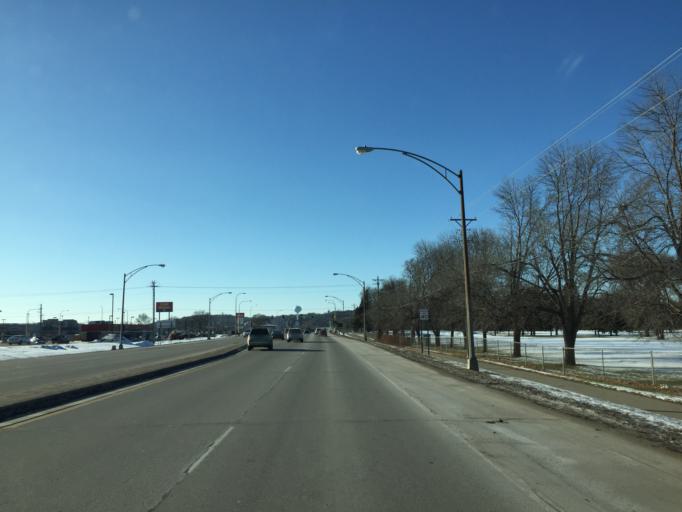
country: US
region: Minnesota
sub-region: Olmsted County
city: Rochester
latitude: 44.0071
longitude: -92.4652
